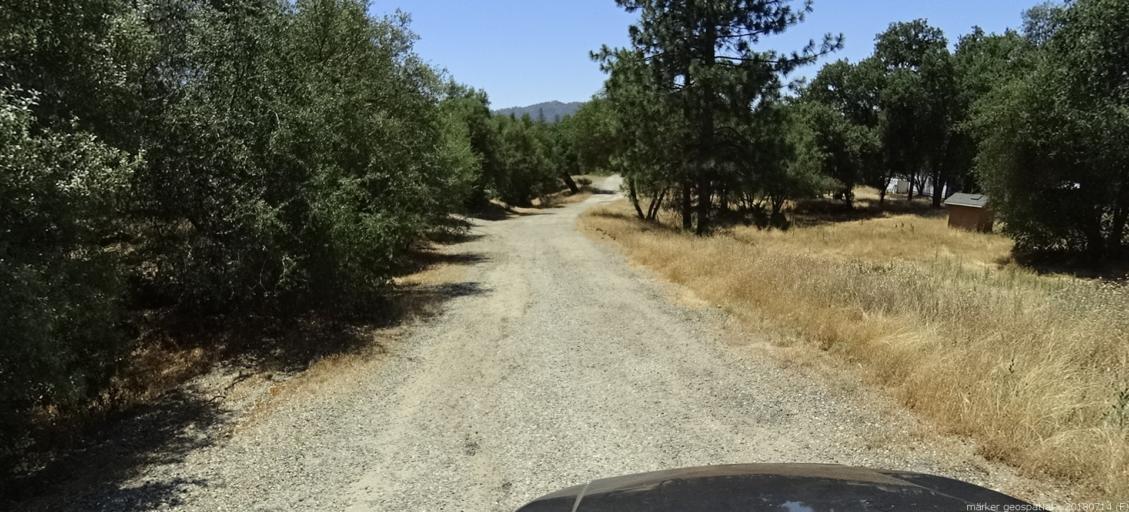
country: US
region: California
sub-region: Madera County
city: Ahwahnee
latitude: 37.3727
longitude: -119.7146
